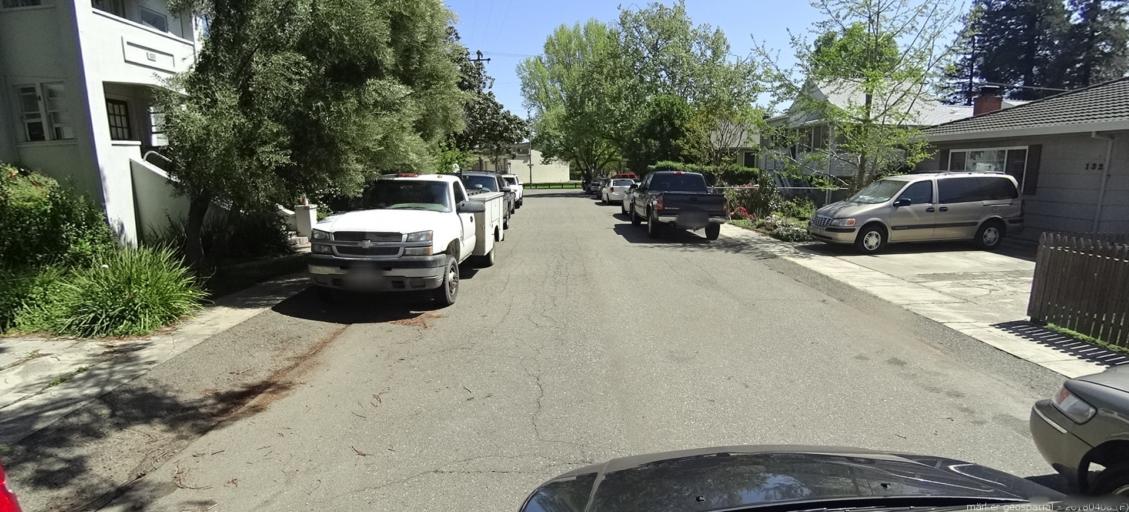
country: US
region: California
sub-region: Sacramento County
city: Walnut Grove
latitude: 38.3308
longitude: -121.5700
